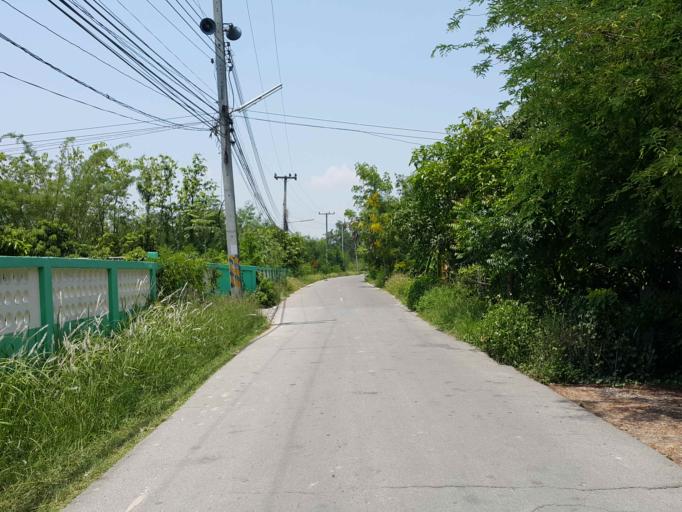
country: TH
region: Chiang Mai
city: San Sai
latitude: 18.8327
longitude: 99.1003
